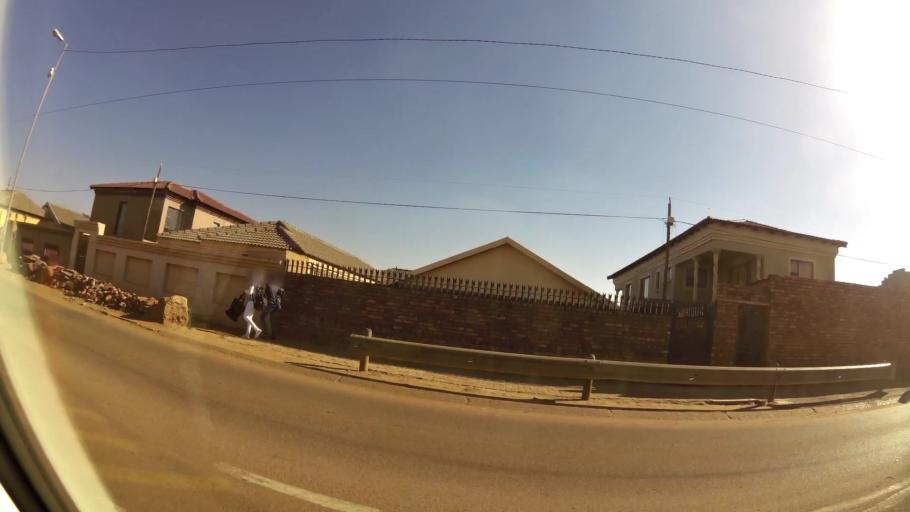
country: ZA
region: Gauteng
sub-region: City of Tshwane Metropolitan Municipality
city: Cullinan
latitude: -25.7172
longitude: 28.3760
